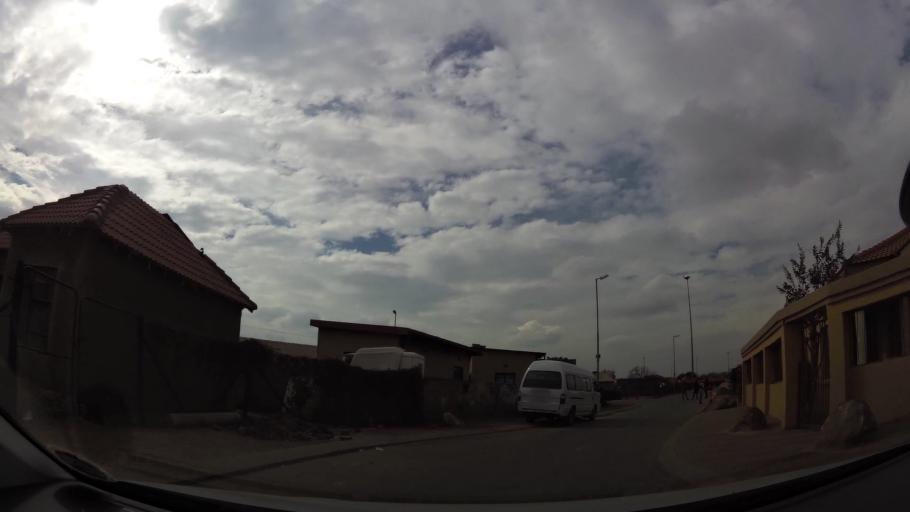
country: ZA
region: Gauteng
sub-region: City of Johannesburg Metropolitan Municipality
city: Soweto
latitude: -26.2693
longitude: 27.8553
